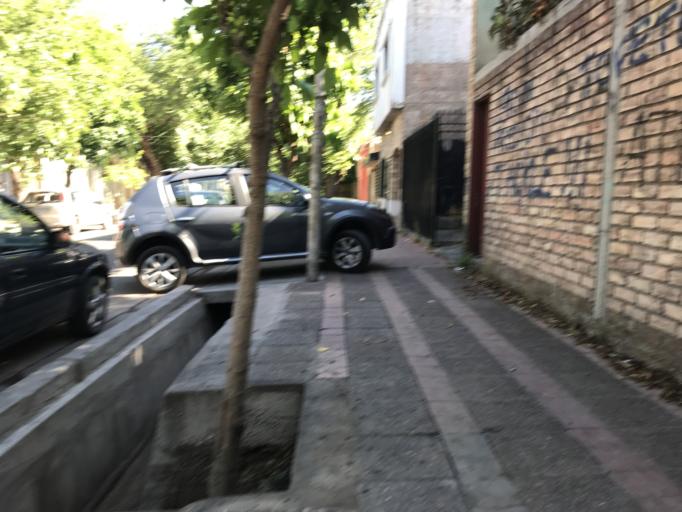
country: AR
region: Mendoza
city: Mendoza
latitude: -32.8777
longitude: -68.8308
